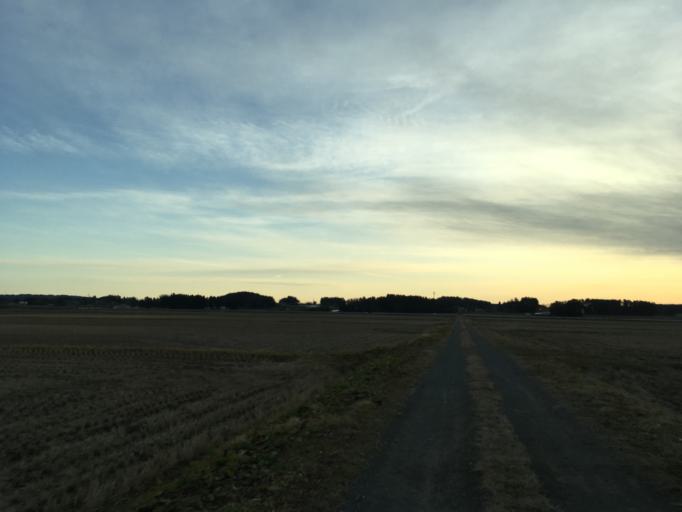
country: JP
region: Miyagi
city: Kogota
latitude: 38.6477
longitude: 141.0642
